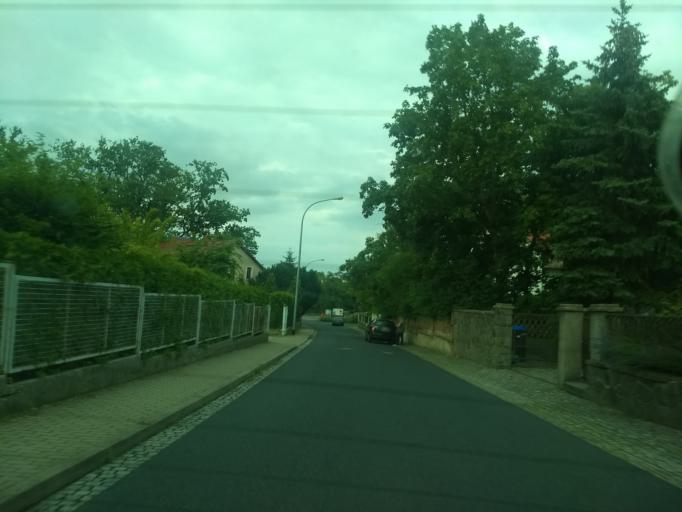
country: DE
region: Saxony
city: Radeburg
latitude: 51.2099
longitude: 13.7260
